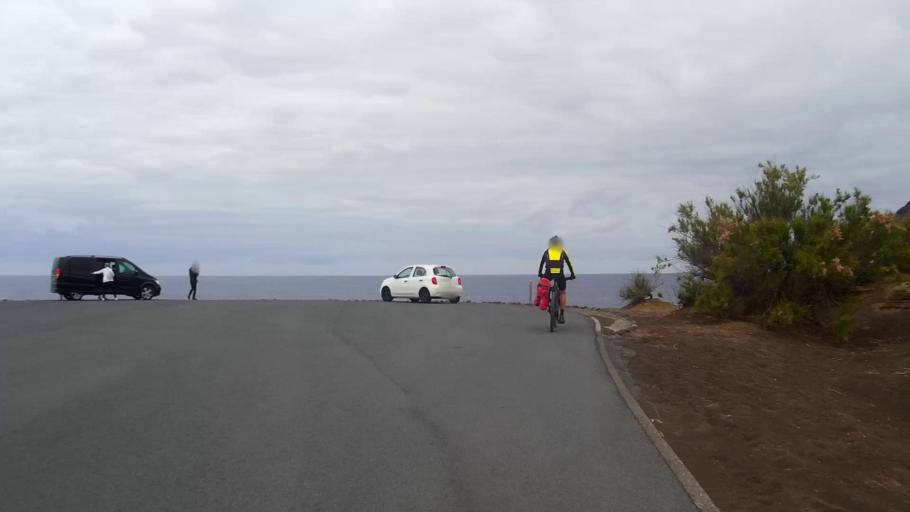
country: PT
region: Azores
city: Ribeira Grande
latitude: 38.5928
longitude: -28.8267
